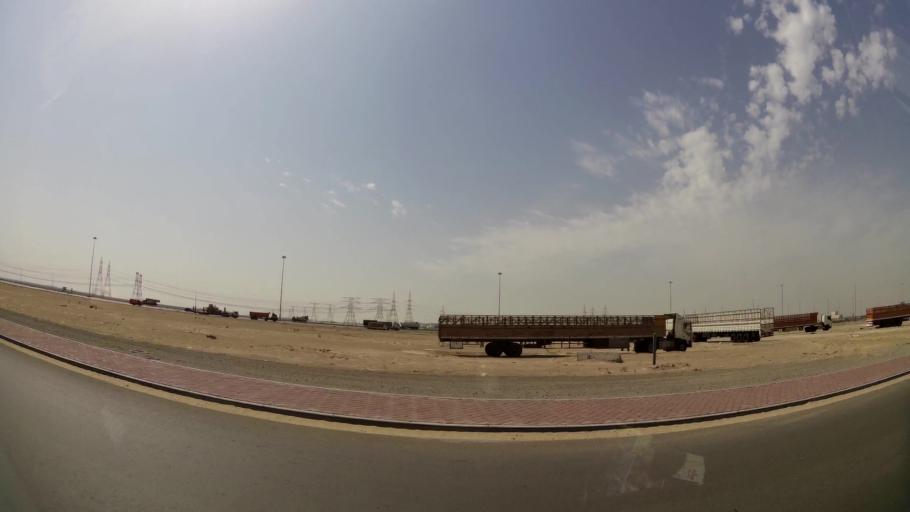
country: AE
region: Abu Dhabi
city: Abu Dhabi
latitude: 24.3097
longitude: 54.5307
